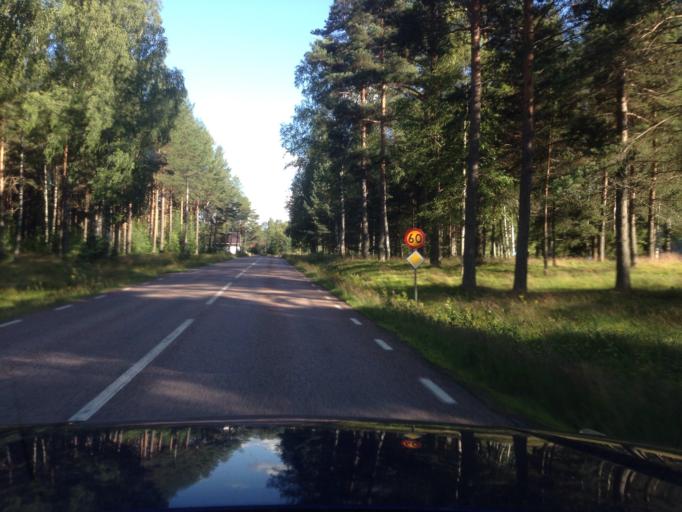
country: SE
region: Dalarna
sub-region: Ludvika Kommun
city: Grangesberg
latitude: 60.1515
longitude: 14.9784
